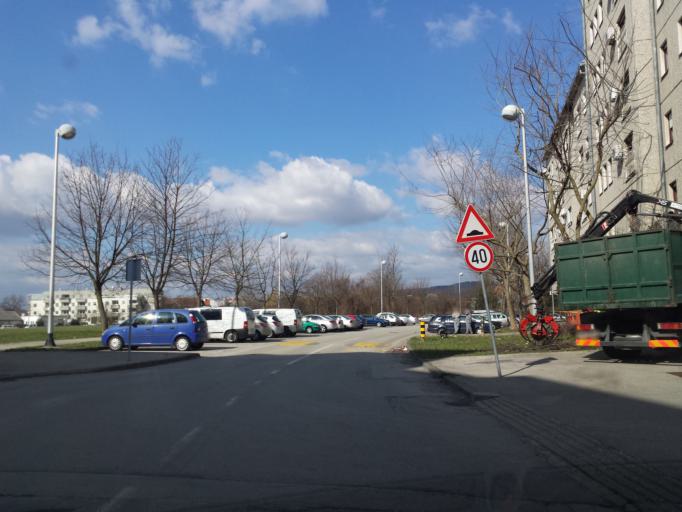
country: HR
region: Grad Zagreb
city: Stenjevec
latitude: 45.8088
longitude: 15.8902
